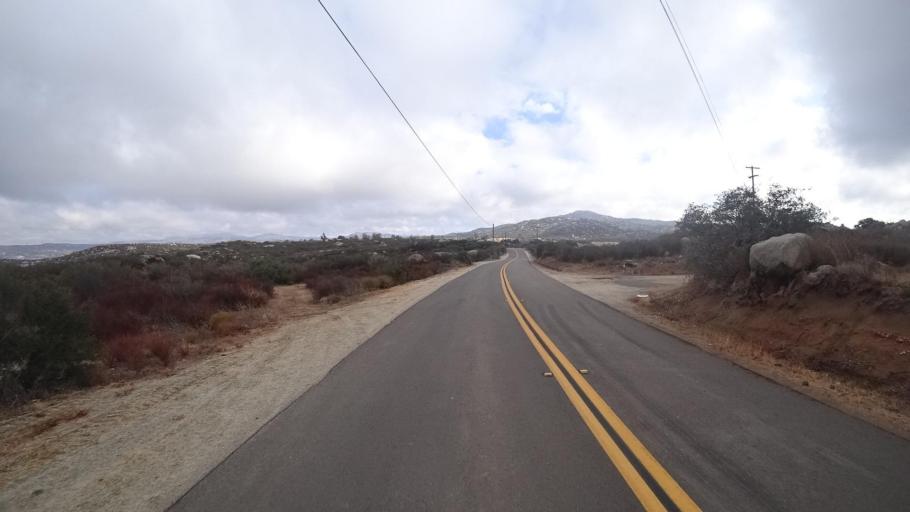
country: MX
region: Baja California
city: Tecate
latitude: 32.6045
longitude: -116.5789
